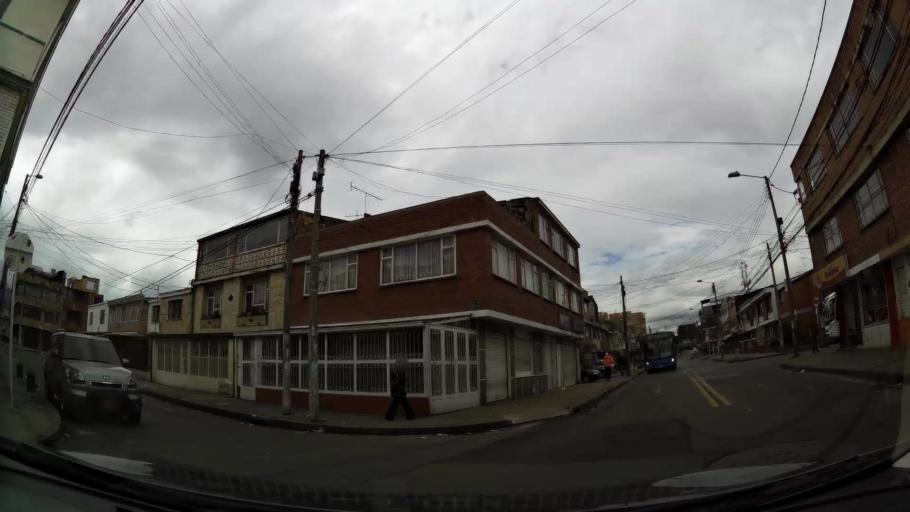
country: CO
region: Bogota D.C.
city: Barrio San Luis
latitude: 4.6861
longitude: -74.0918
